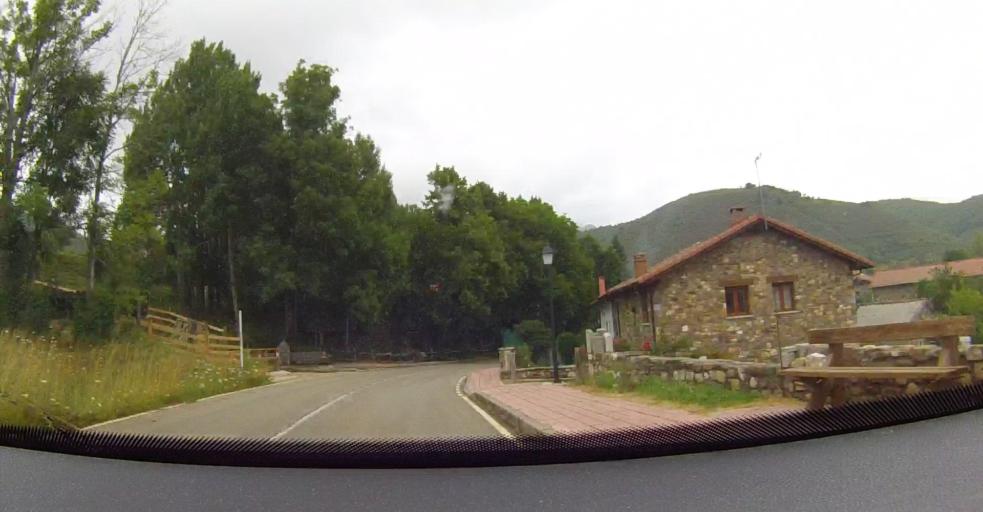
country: ES
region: Castille and Leon
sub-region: Provincia de Leon
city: Acebedo
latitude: 43.0395
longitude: -5.0953
